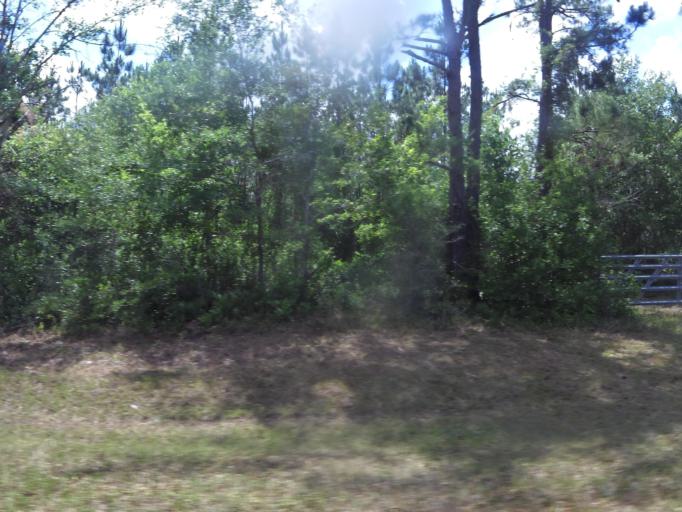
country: US
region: Florida
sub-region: Clay County
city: Green Cove Springs
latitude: 29.9532
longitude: -81.7392
